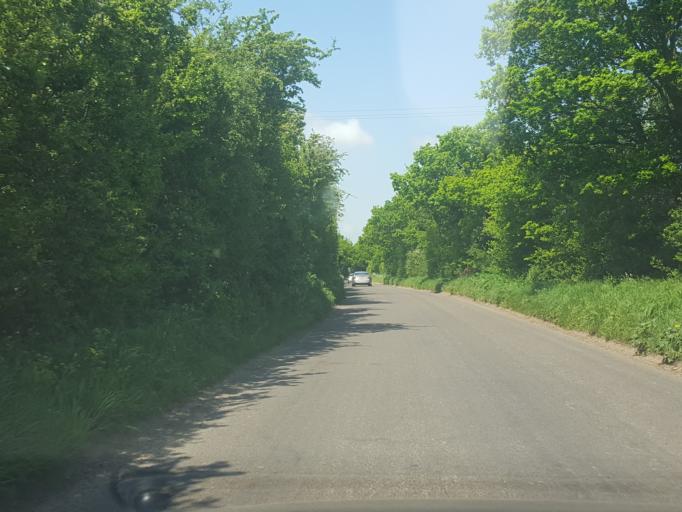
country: GB
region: England
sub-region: Essex
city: Great Bentley
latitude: 51.8533
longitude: 1.0423
